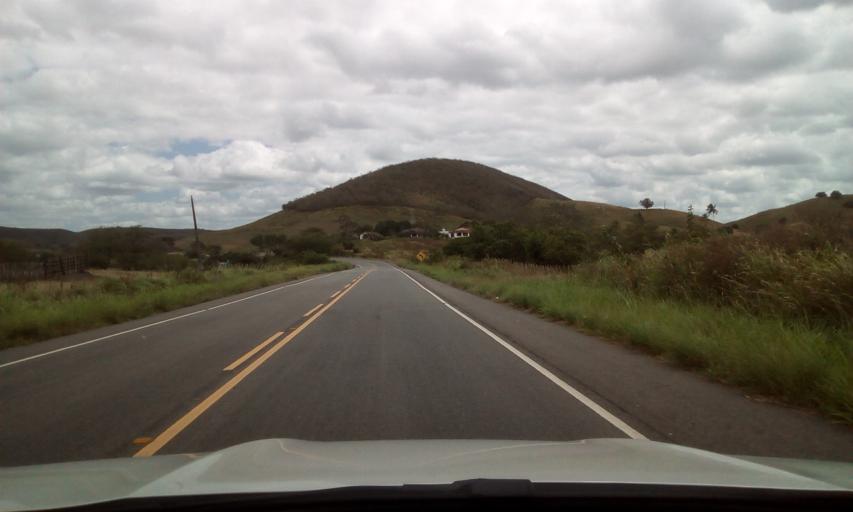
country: BR
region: Paraiba
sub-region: Serra Redonda
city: Alagoa Grande
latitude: -7.1188
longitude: -35.6148
